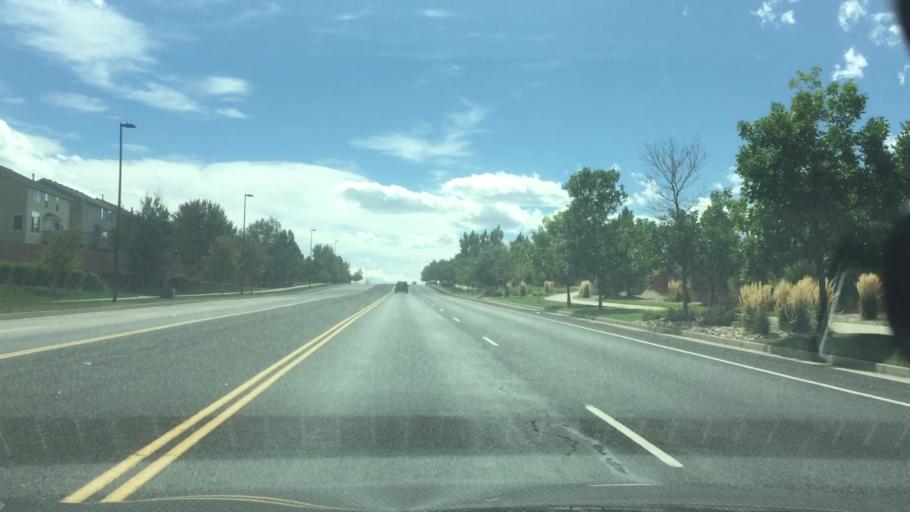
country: US
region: Colorado
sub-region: Arapahoe County
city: Dove Valley
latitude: 39.6444
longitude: -104.7351
